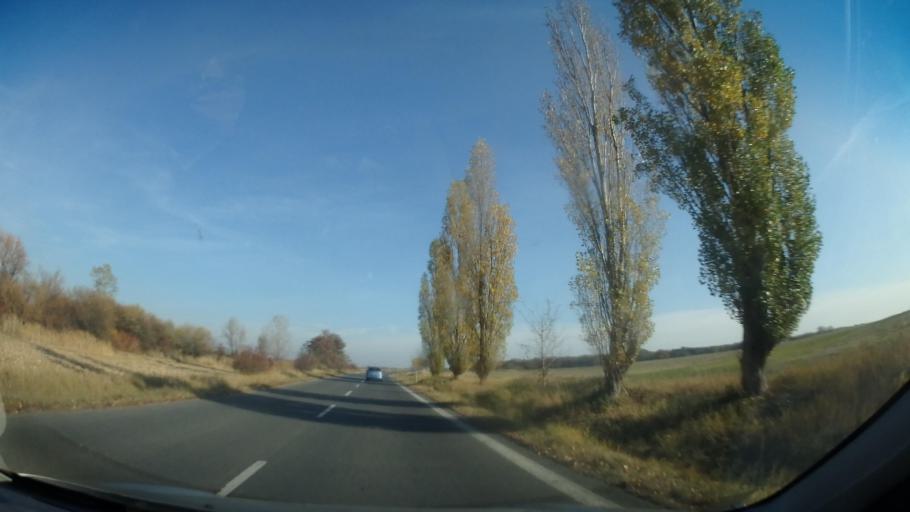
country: CZ
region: Praha
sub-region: Praha 20
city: Horni Pocernice
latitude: 50.0627
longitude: 14.6185
